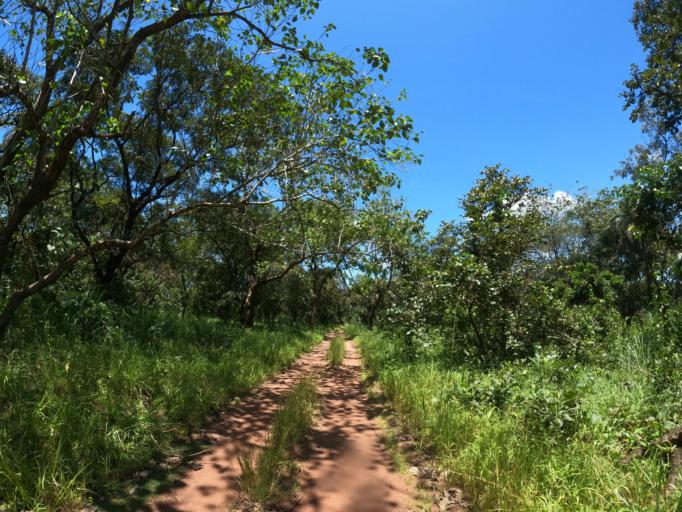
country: SL
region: Northern Province
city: Makeni
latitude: 9.1055
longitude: -12.2507
